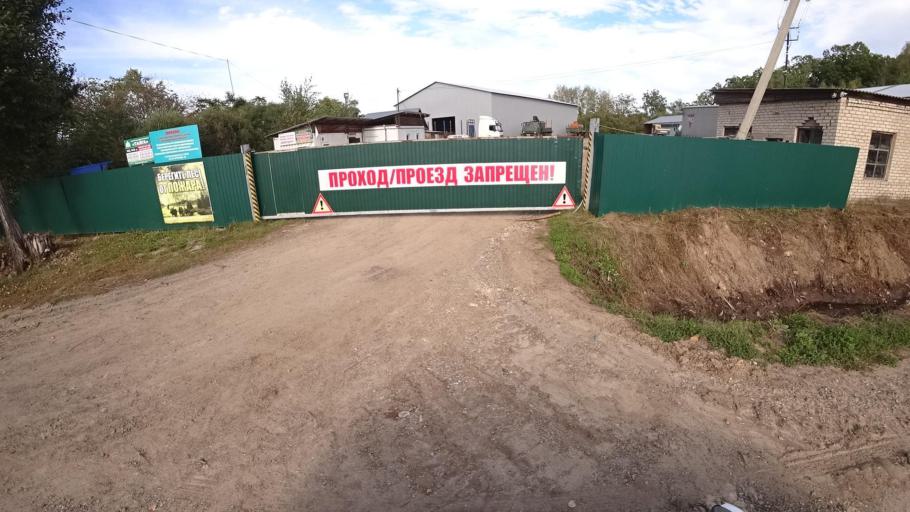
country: RU
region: Primorskiy
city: Dostoyevka
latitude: 44.3070
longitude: 133.4663
